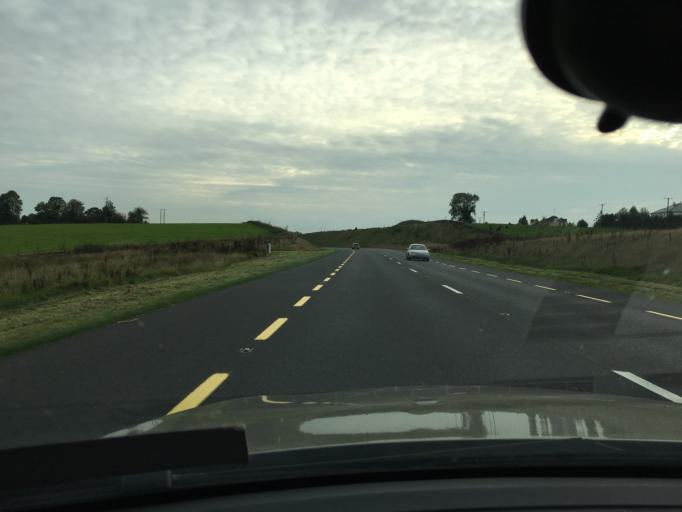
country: IE
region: Leinster
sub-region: An Longfort
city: Longford
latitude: 53.7318
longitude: -7.8228
